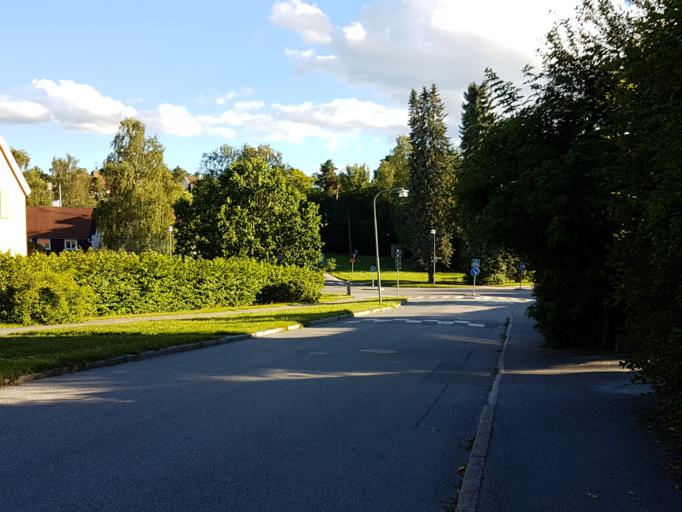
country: SE
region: Stockholm
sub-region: Stockholms Kommun
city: Bromma
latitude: 59.3257
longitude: 17.9710
